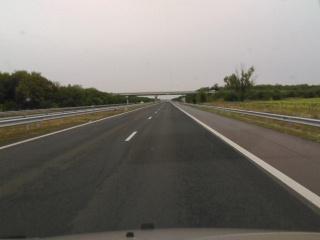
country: BG
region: Stara Zagora
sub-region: Obshtina Stara Zagora
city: Stara Zagora
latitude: 42.3433
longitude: 25.6868
